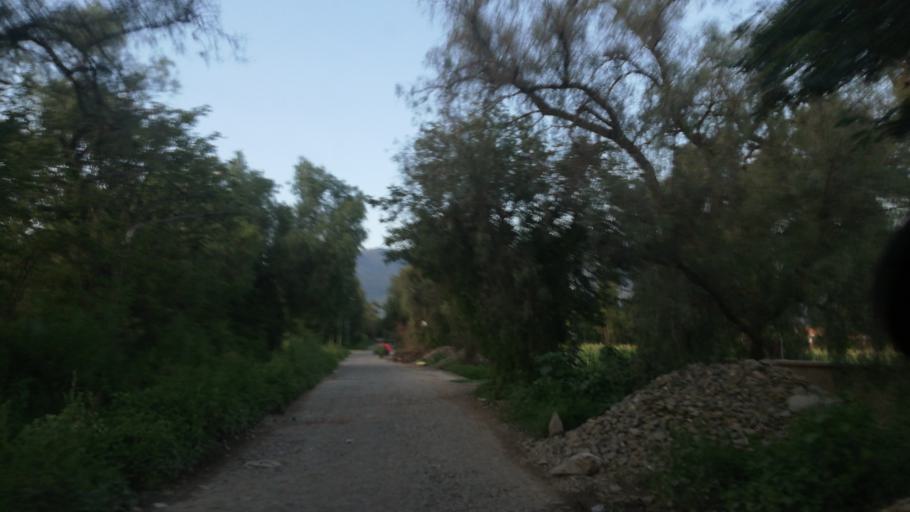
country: BO
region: Cochabamba
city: Cochabamba
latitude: -17.3737
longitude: -66.2074
